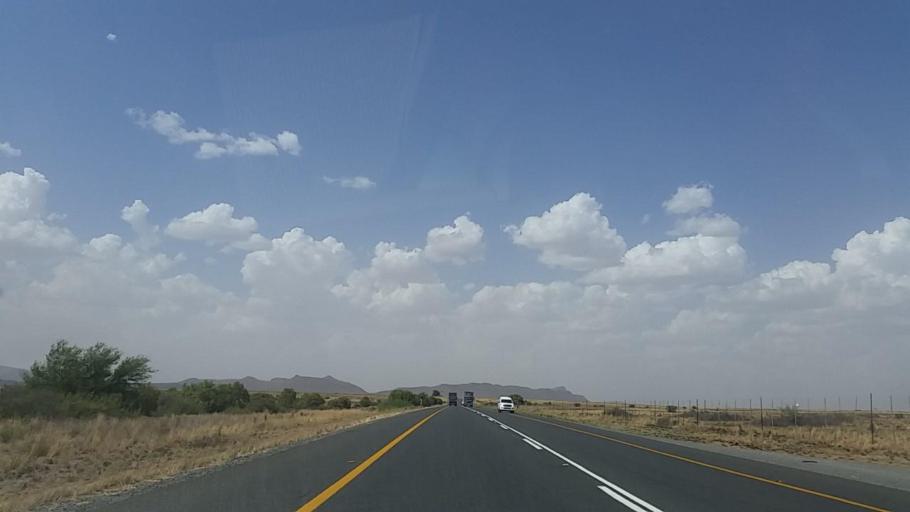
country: ZA
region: Northern Cape
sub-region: Pixley ka Seme District Municipality
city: Colesberg
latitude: -30.5723
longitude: 25.4513
